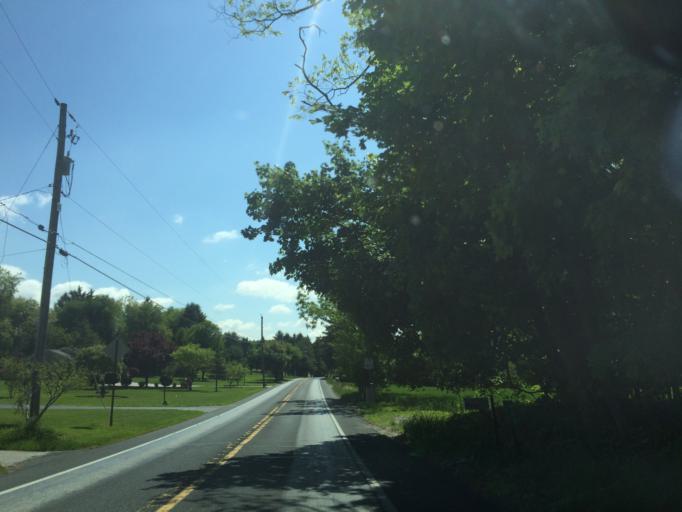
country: US
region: Pennsylvania
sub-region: York County
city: Parkville
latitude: 39.7938
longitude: -76.9348
